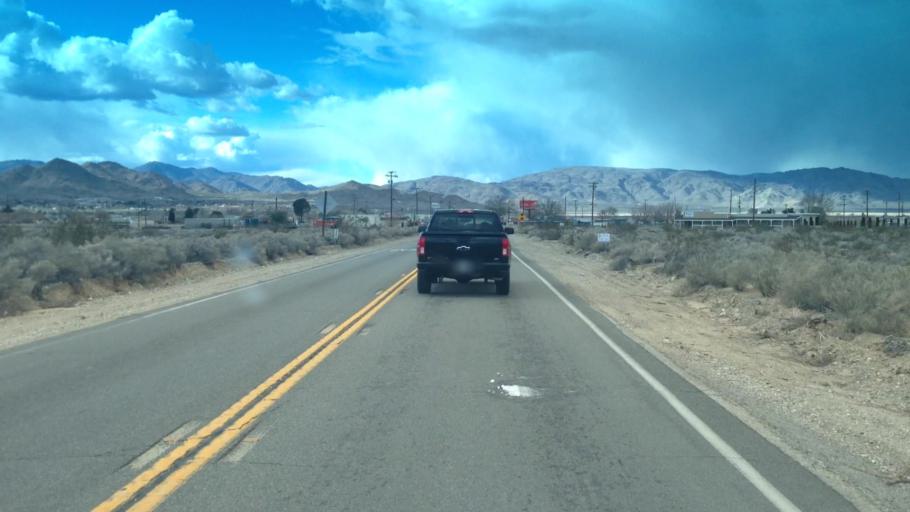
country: US
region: California
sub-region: San Bernardino County
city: Lucerne Valley
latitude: 34.4399
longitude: -116.9457
